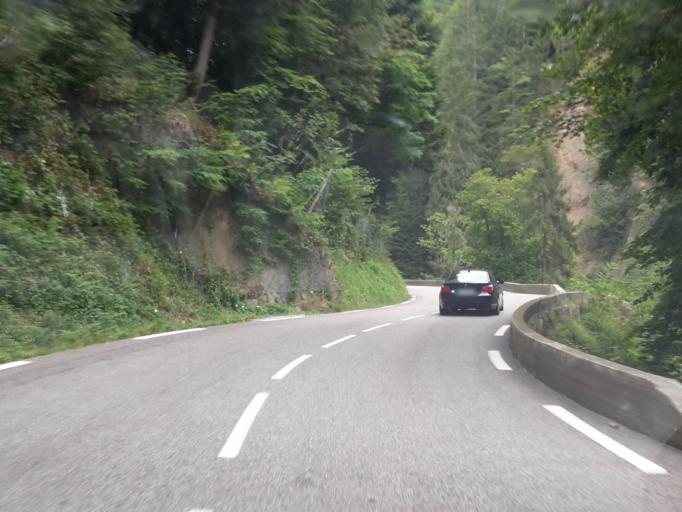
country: FR
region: Rhone-Alpes
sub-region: Departement de la Savoie
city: Ugine
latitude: 45.7760
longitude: 6.4861
